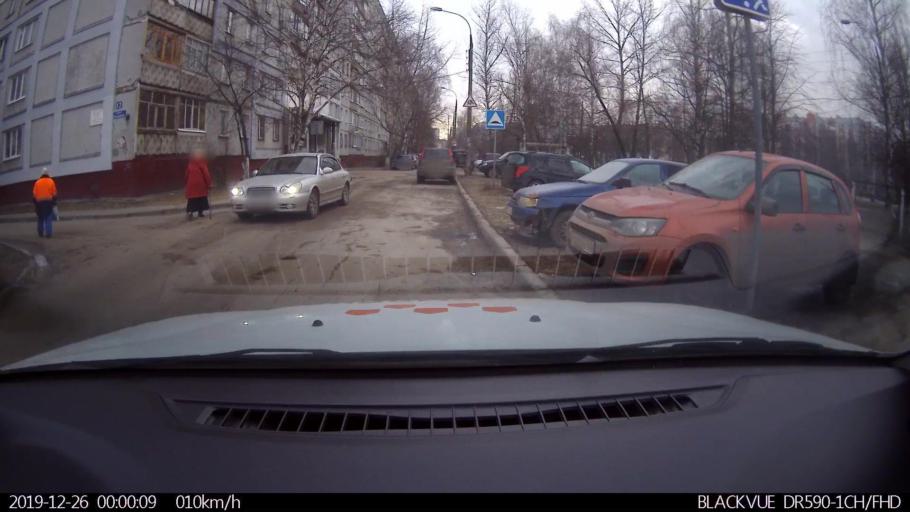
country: RU
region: Nizjnij Novgorod
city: Gorbatovka
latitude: 56.2631
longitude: 43.8479
